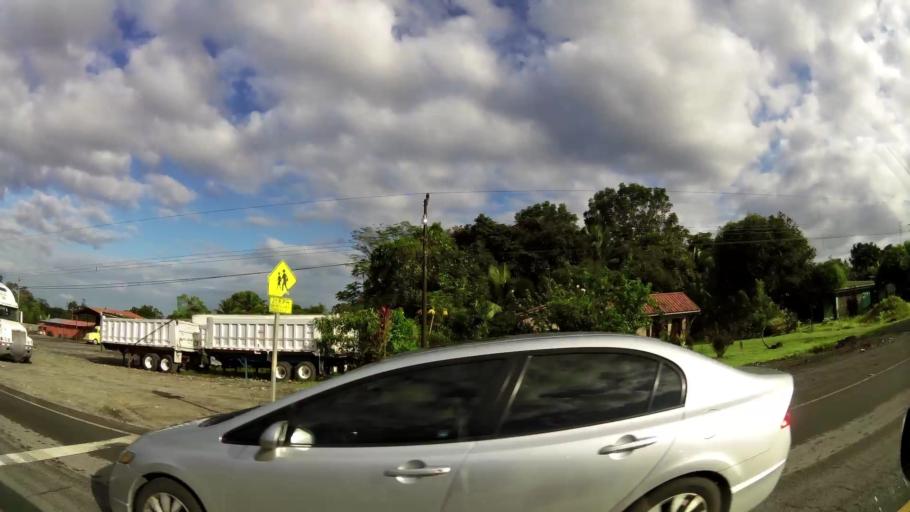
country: CR
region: Limon
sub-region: Canton de Pococi
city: Guapiles
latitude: 10.2128
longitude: -83.8461
